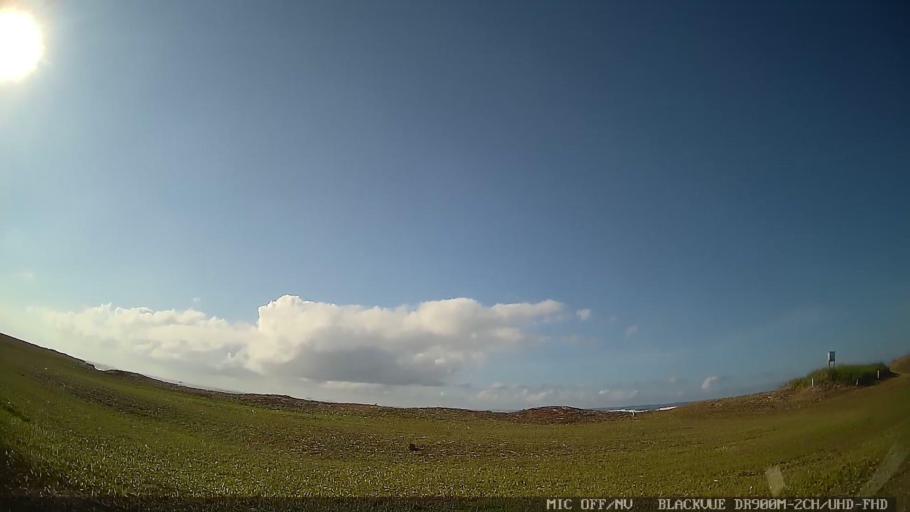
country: BR
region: Sao Paulo
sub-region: Peruibe
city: Peruibe
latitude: -24.2779
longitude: -46.9391
